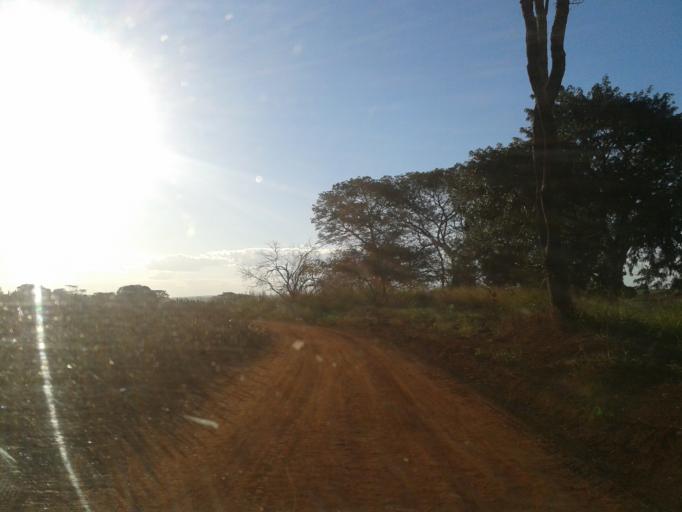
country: BR
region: Minas Gerais
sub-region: Centralina
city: Centralina
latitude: -18.6091
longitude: -49.3031
